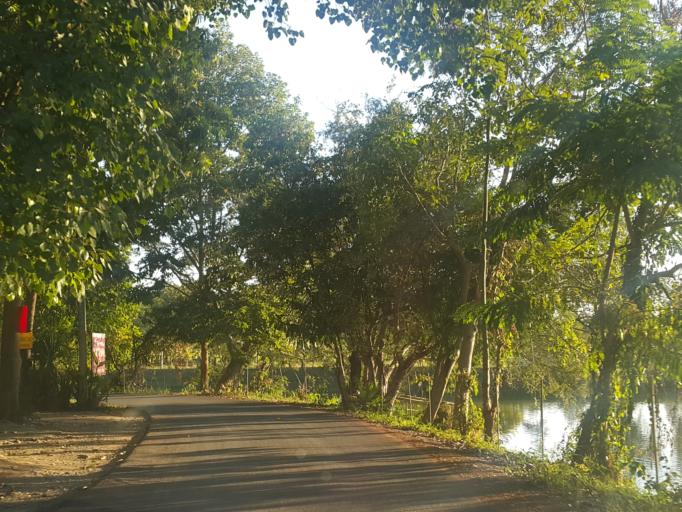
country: TH
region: Chiang Mai
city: San Sai
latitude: 18.8740
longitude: 99.1555
